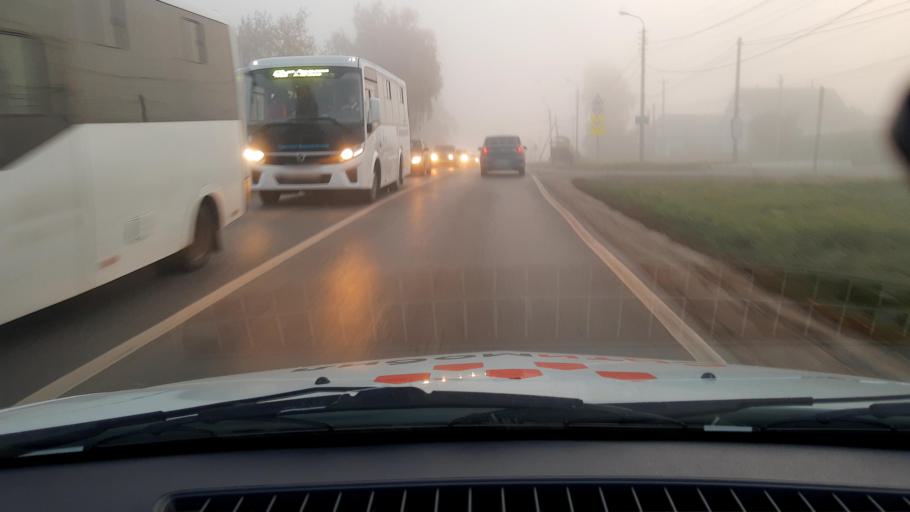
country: RU
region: Bashkortostan
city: Iglino
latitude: 54.7848
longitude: 56.2278
